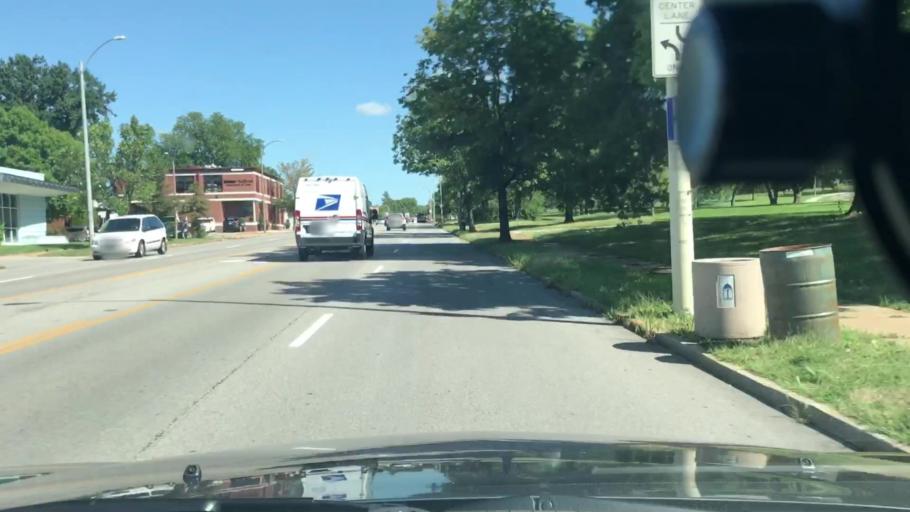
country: US
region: Missouri
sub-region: Saint Louis County
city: Maplewood
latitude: 38.5996
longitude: -90.2923
